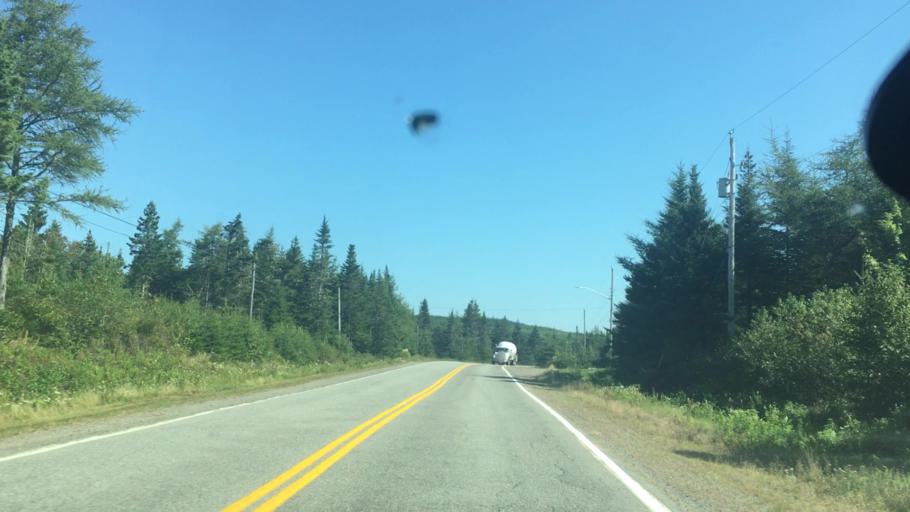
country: CA
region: Nova Scotia
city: New Glasgow
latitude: 44.9024
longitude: -62.4145
